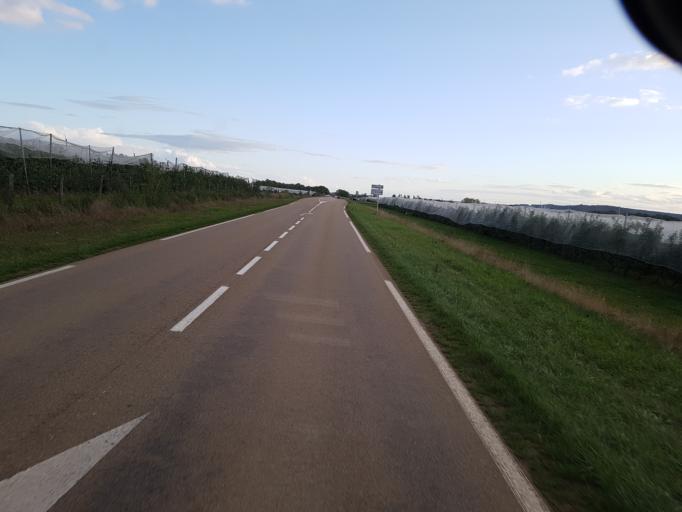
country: FR
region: Bourgogne
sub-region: Departement de l'Yonne
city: Saint-Clement
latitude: 48.2499
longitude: 3.2849
